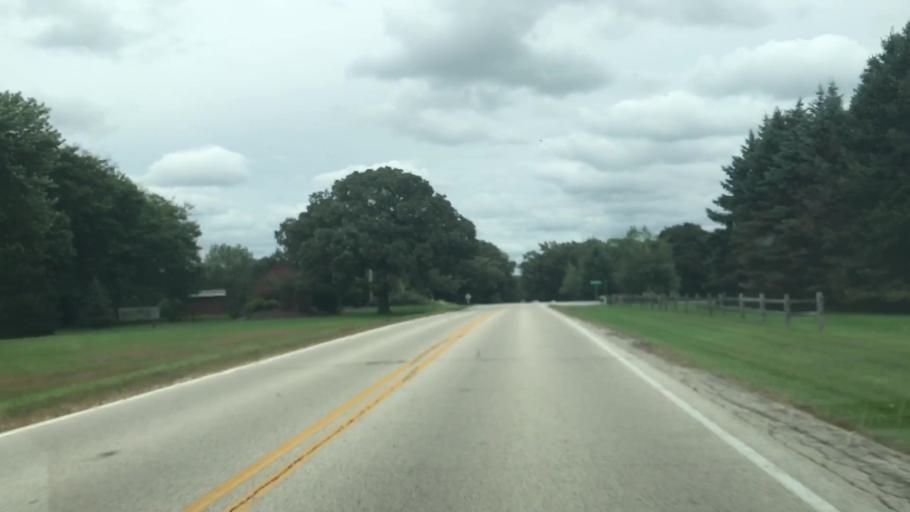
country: US
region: Wisconsin
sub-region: Waukesha County
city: North Prairie
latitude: 42.9003
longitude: -88.4044
